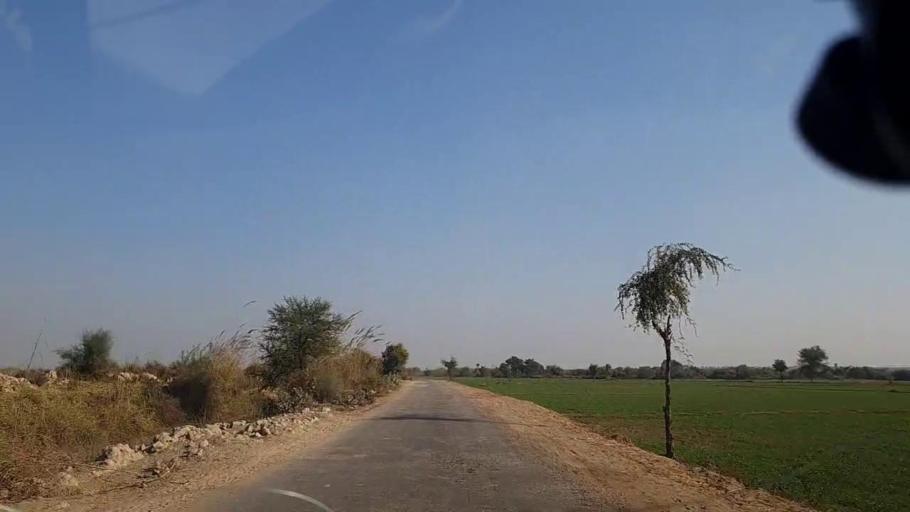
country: PK
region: Sindh
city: Khanpur
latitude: 27.6833
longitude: 69.5312
